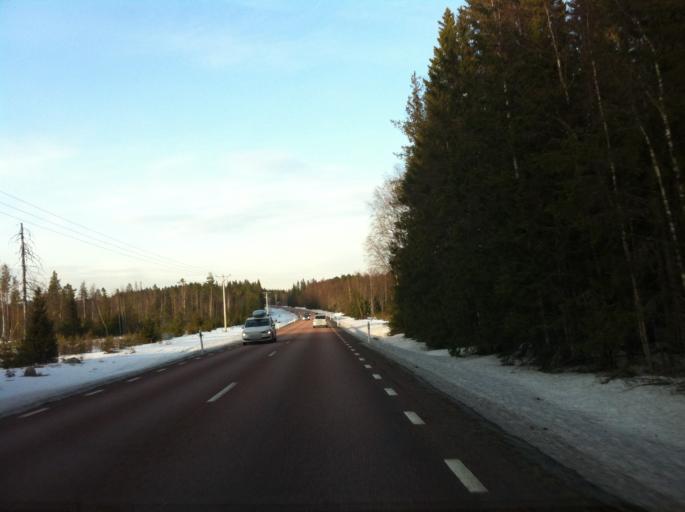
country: SE
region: Dalarna
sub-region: Vansbro Kommun
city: Vansbro
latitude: 60.2947
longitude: 14.1826
